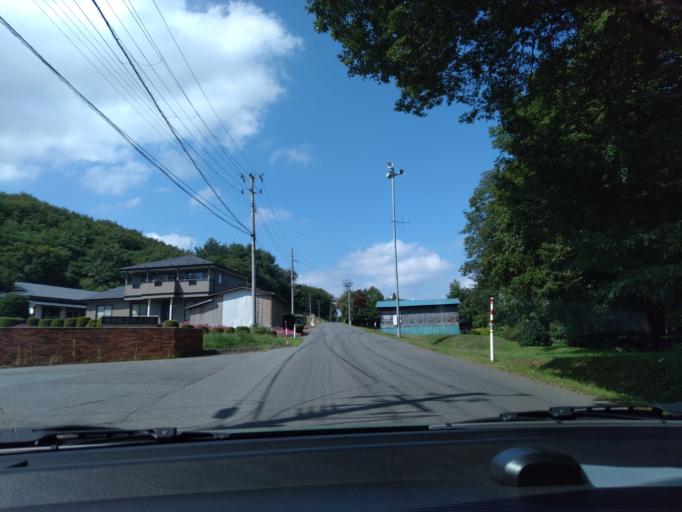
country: JP
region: Iwate
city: Shizukuishi
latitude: 39.6688
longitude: 140.9692
